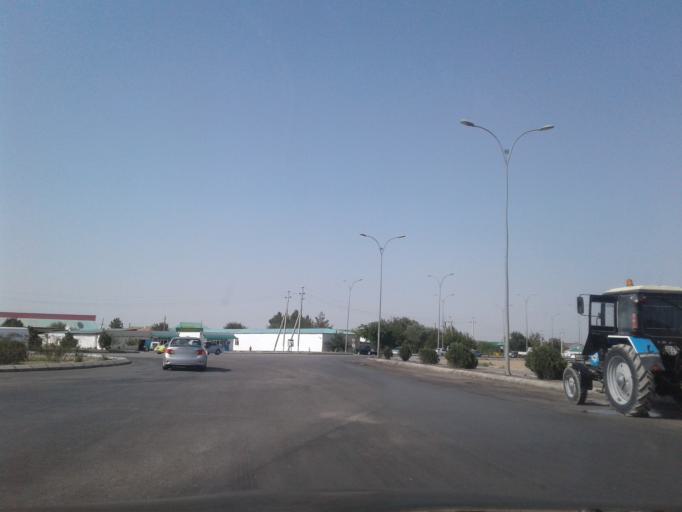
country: TM
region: Ahal
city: Ashgabat
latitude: 37.9694
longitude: 58.4228
